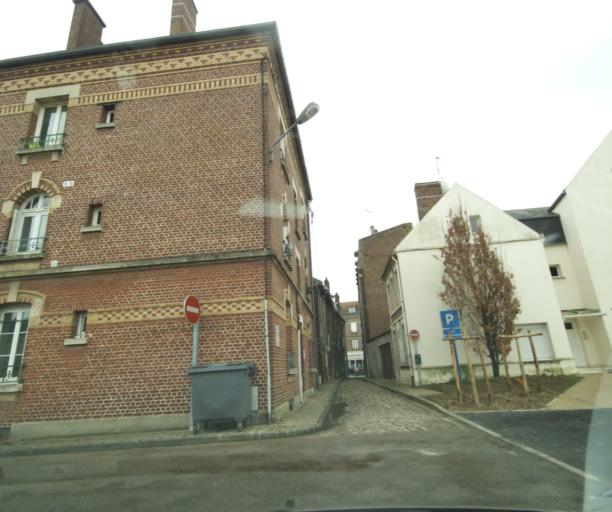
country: FR
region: Picardie
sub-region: Departement de l'Oise
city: Noyon
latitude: 49.5810
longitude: 2.9974
